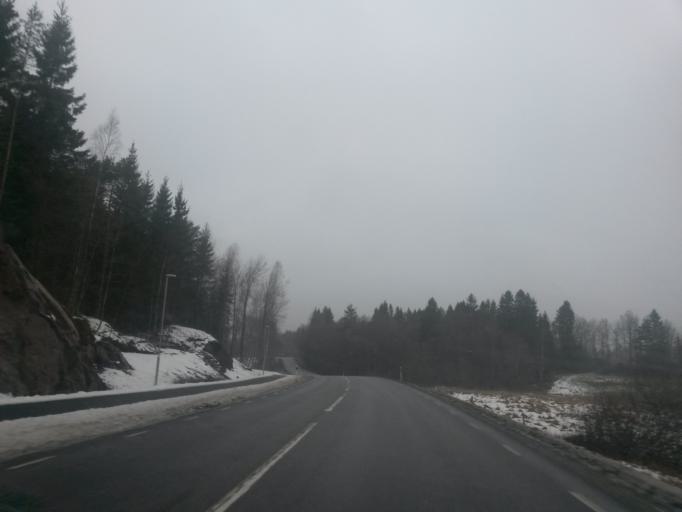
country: SE
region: Vaestra Goetaland
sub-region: Alingsas Kommun
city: Sollebrunn
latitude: 58.1120
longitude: 12.5768
